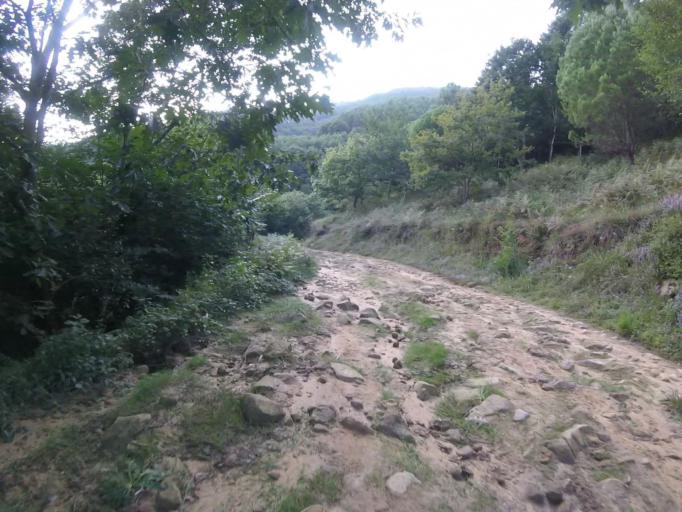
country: ES
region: Basque Country
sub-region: Provincia de Guipuzcoa
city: Lezo
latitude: 43.3418
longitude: -1.8500
